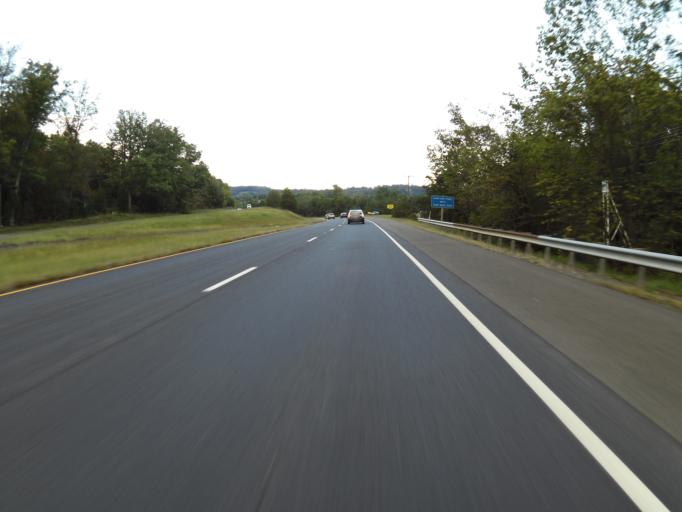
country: US
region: Virginia
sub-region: Fauquier County
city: Warrenton
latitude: 38.6790
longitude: -77.9106
